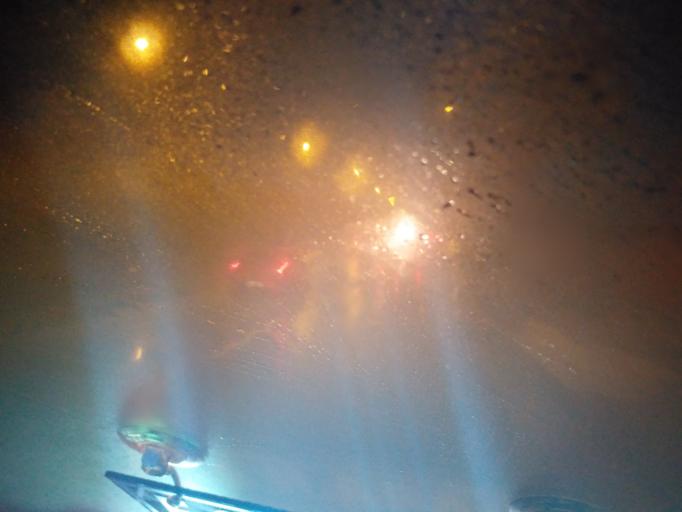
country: TR
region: Ankara
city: Ankara
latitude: 39.9591
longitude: 32.8232
